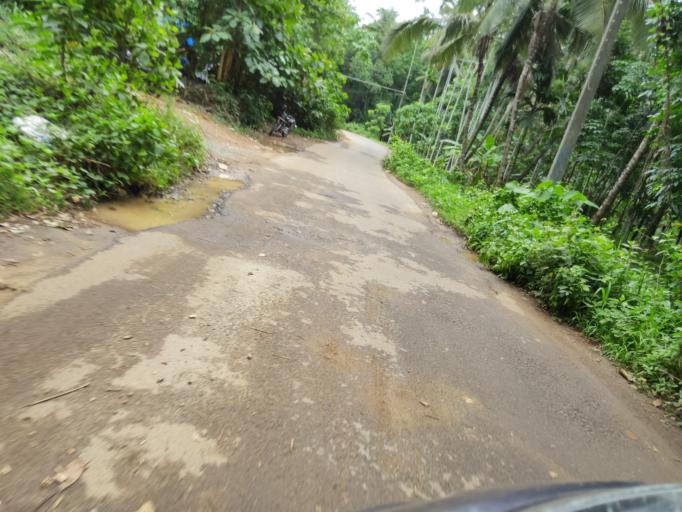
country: IN
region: Kerala
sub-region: Malappuram
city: Manjeri
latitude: 11.2216
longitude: 76.2529
